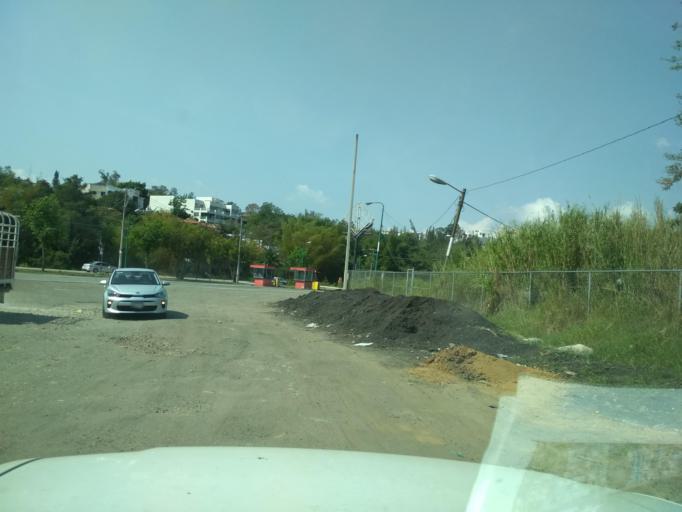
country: MX
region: Veracruz
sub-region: Emiliano Zapata
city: Las Trancas
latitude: 19.5145
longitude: -96.8569
